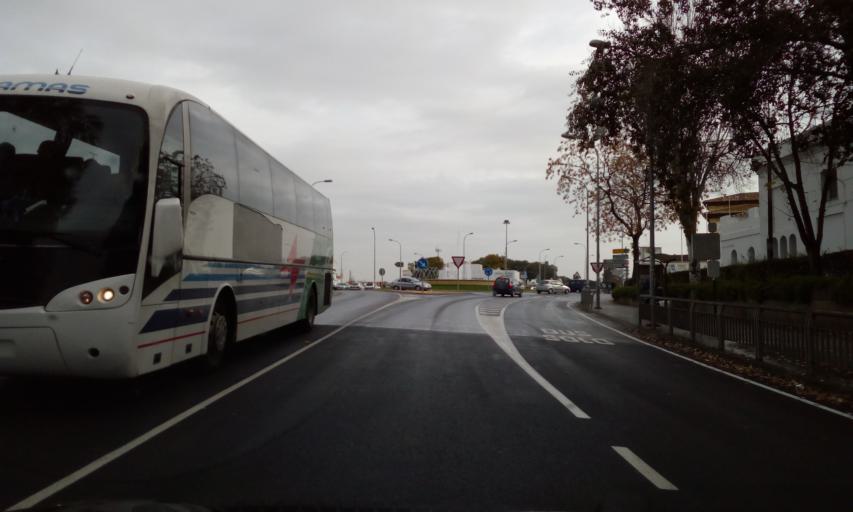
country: ES
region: Andalusia
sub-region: Provincia de Huelva
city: Cartaya
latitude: 37.2886
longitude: -7.1518
